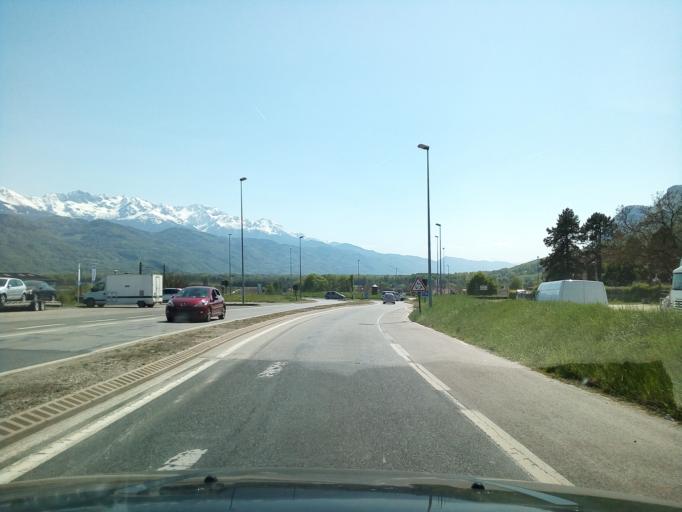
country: FR
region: Rhone-Alpes
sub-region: Departement de l'Isere
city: Le Touvet
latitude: 45.3584
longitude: 5.9555
